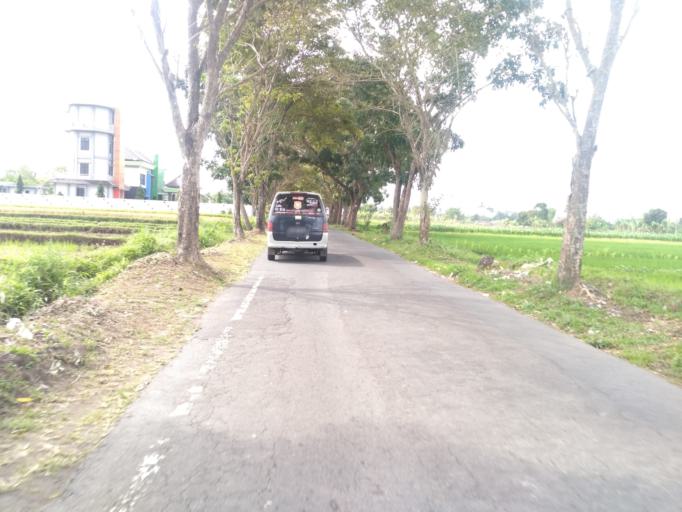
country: ID
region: Daerah Istimewa Yogyakarta
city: Melati
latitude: -7.7327
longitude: 110.3542
